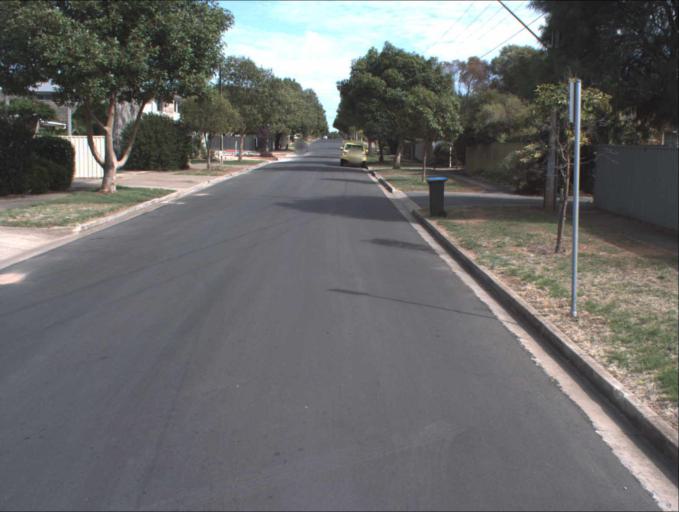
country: AU
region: South Australia
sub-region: Port Adelaide Enfield
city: Klemzig
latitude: -34.8800
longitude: 138.6340
